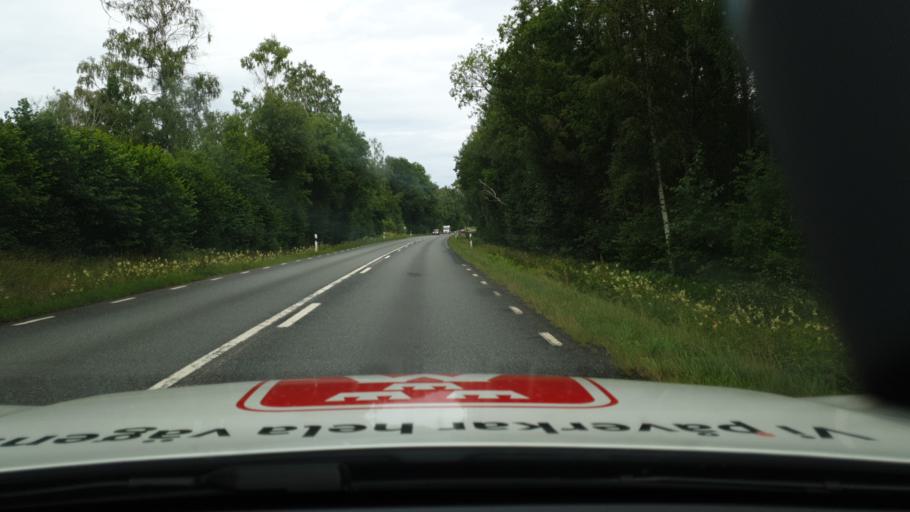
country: SE
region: Vaestra Goetaland
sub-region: Hjo Kommun
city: Hjo
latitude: 58.1154
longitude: 14.2107
